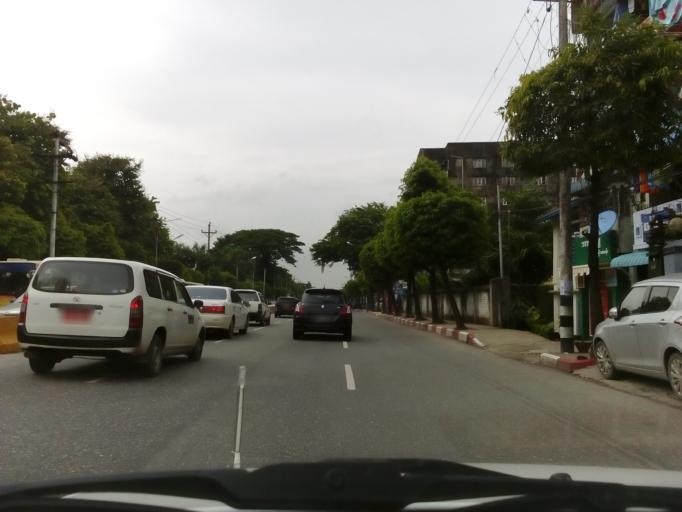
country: MM
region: Yangon
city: Yangon
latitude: 16.8584
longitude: 96.1562
